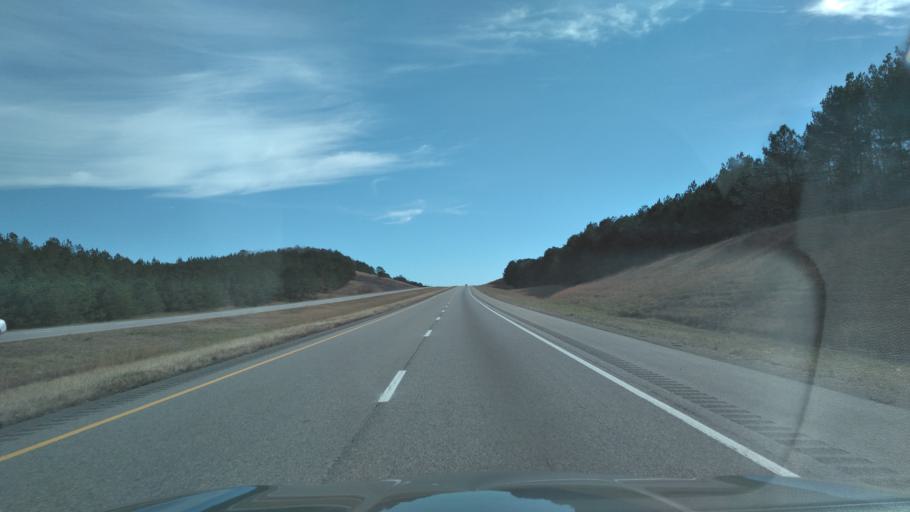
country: US
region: Alabama
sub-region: Marion County
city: Hamilton
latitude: 34.0603
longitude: -87.9499
